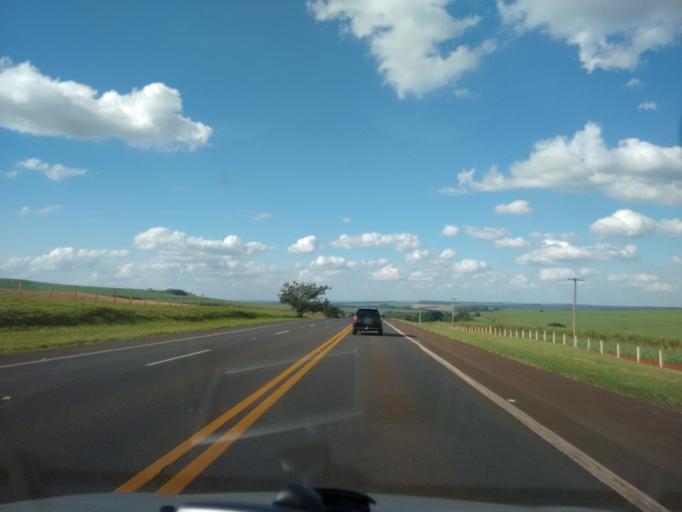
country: BR
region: Sao Paulo
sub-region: Americo Brasiliense
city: Americo Brasiliense
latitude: -21.7639
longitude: -48.0817
